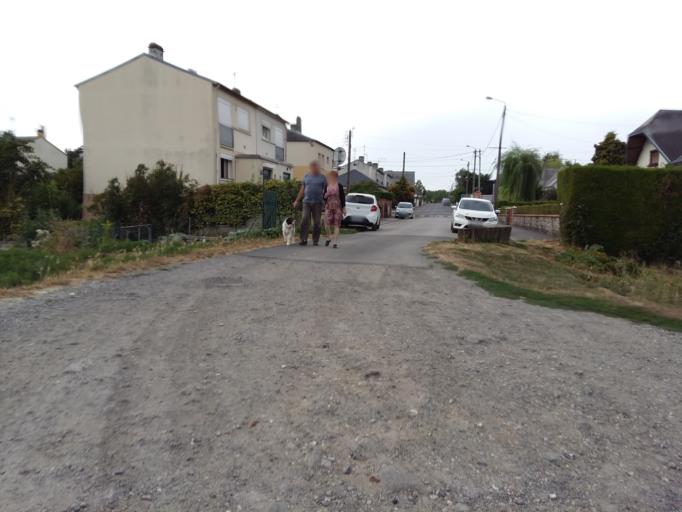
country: FR
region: Picardie
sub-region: Departement de la Somme
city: Camon
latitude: 49.8918
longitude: 2.3438
